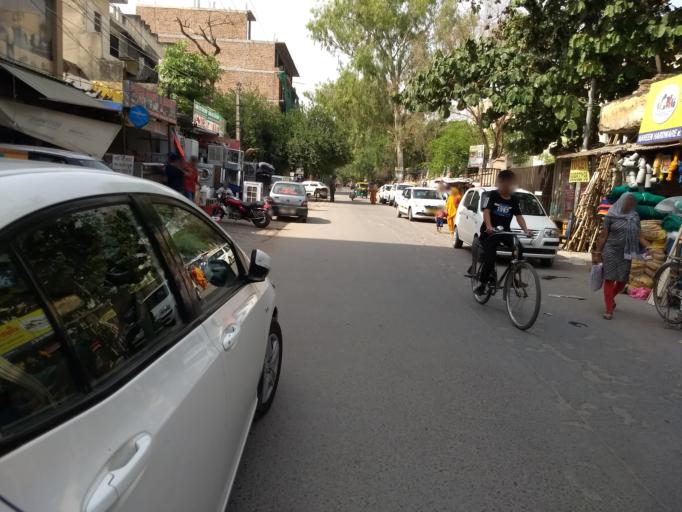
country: IN
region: Haryana
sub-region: Gurgaon
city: Gurgaon
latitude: 28.4771
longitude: 77.0851
